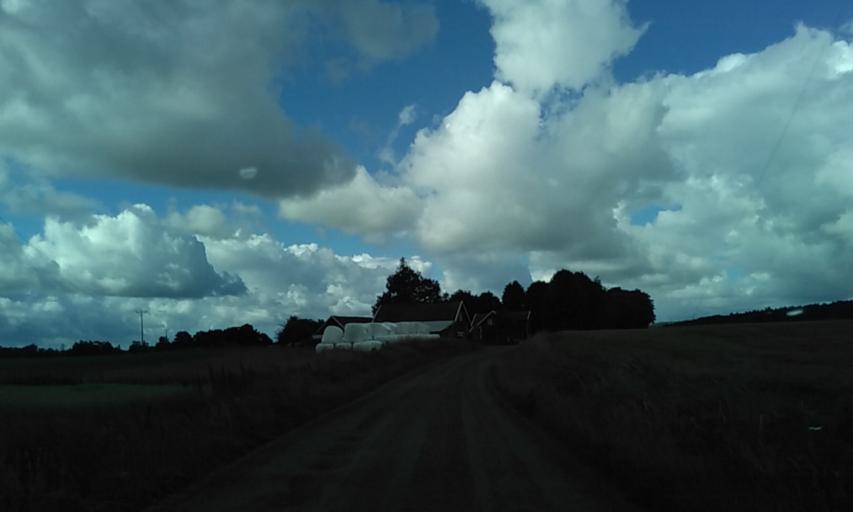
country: SE
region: Vaestra Goetaland
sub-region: Alingsas Kommun
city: Alingsas
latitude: 57.9894
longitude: 12.6145
